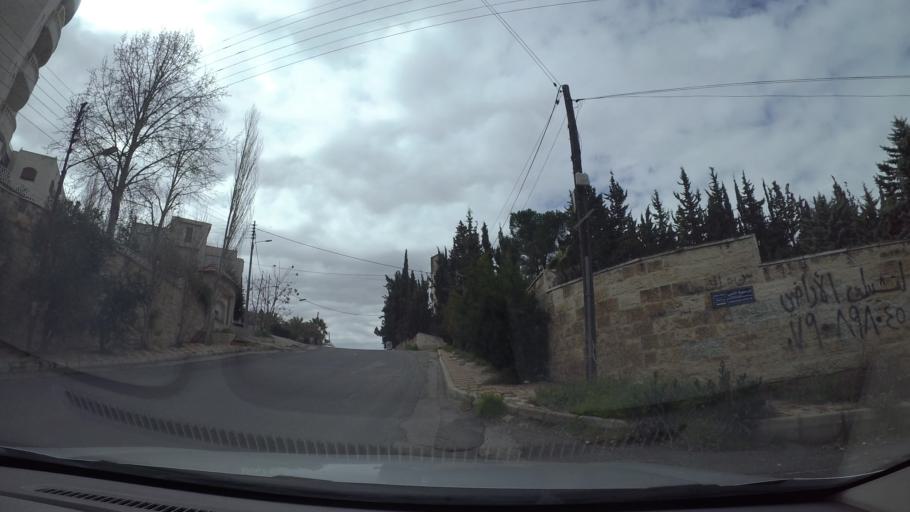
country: JO
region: Amman
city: Al Jubayhah
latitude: 32.0049
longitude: 35.8363
